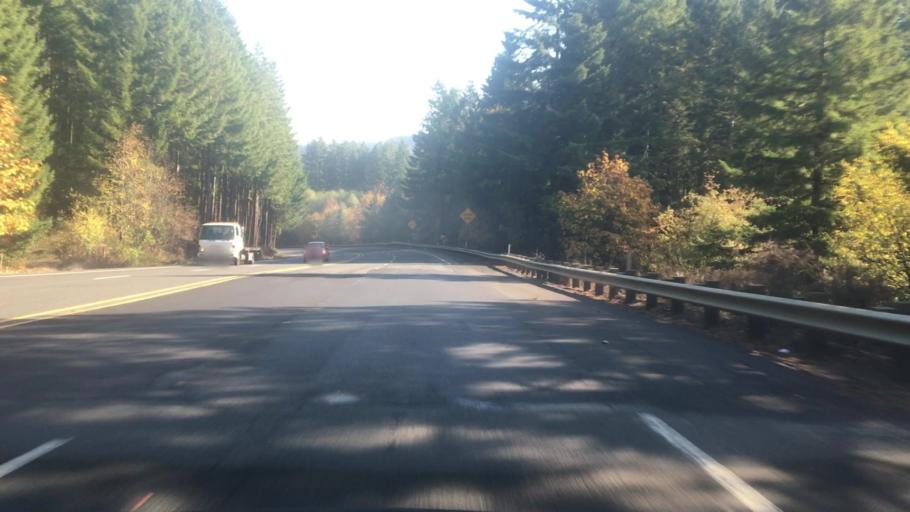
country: US
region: Oregon
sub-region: Polk County
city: Grand Ronde
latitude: 45.0594
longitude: -123.6873
